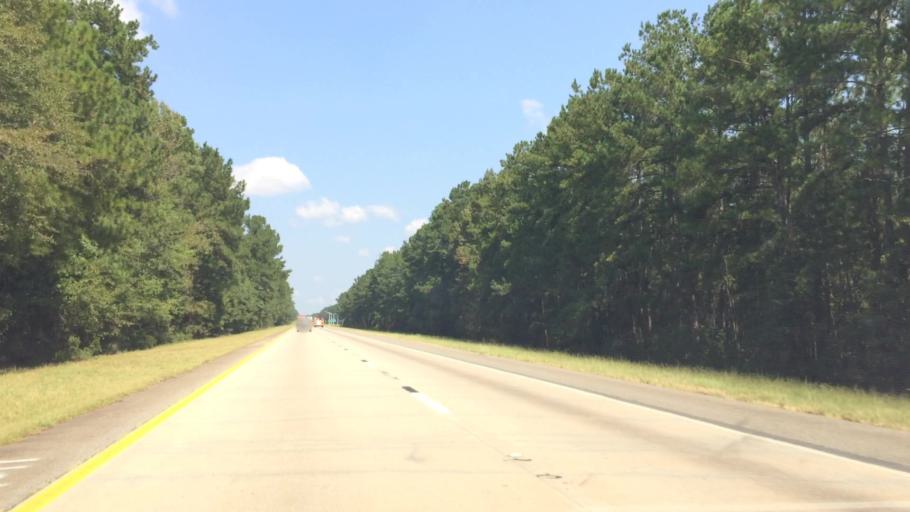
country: US
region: South Carolina
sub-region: Colleton County
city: Walterboro
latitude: 32.9920
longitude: -80.6713
